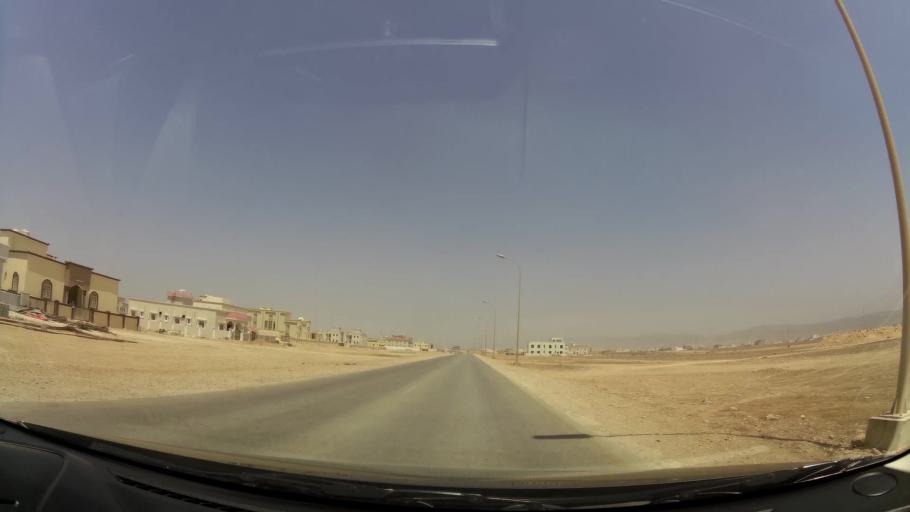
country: OM
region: Zufar
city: Salalah
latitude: 17.0918
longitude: 54.2073
